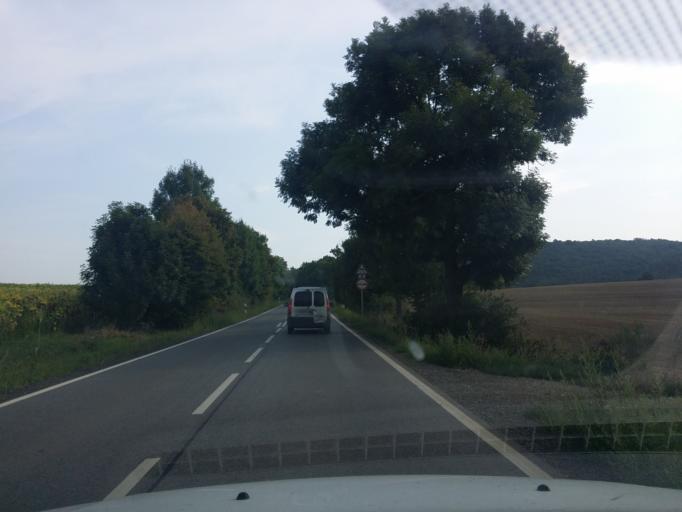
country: HU
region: Pest
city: Acsa
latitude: 47.7850
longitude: 19.3643
